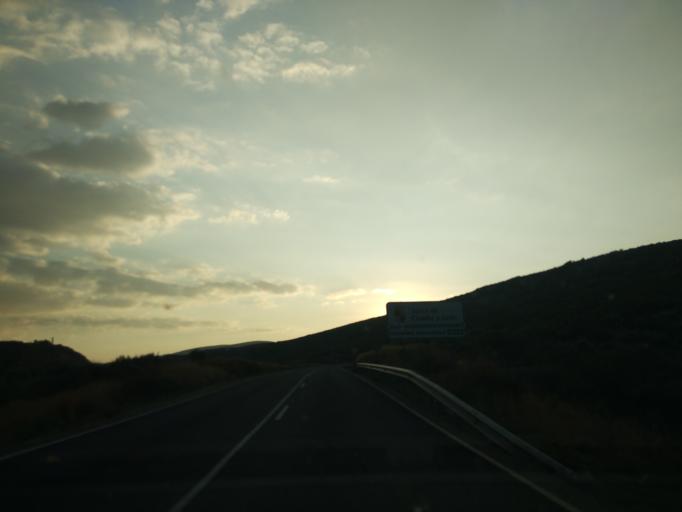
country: ES
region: Castille and Leon
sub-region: Provincia de Avila
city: San Martin del Pimpollar
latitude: 40.3731
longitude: -5.0253
